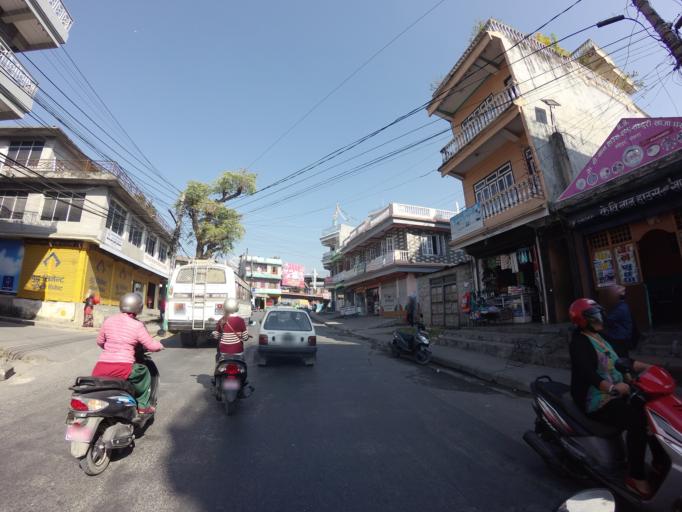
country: NP
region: Western Region
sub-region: Gandaki Zone
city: Pokhara
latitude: 28.2292
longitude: 83.9909
